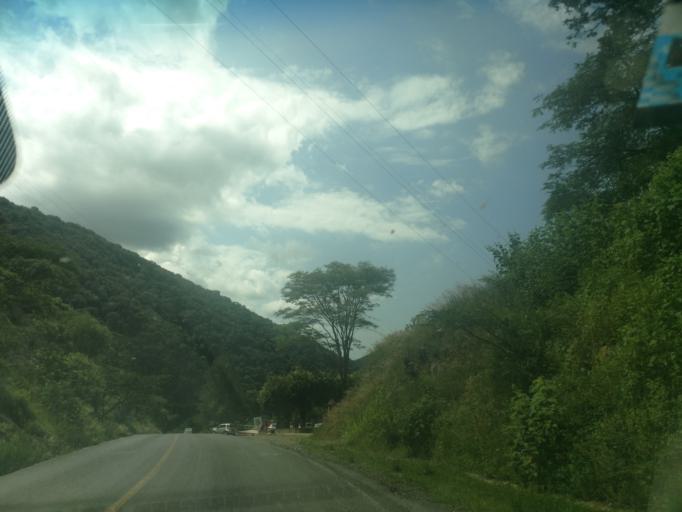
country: MX
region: Jalisco
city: Talpa de Allende
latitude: 20.4206
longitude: -104.8007
